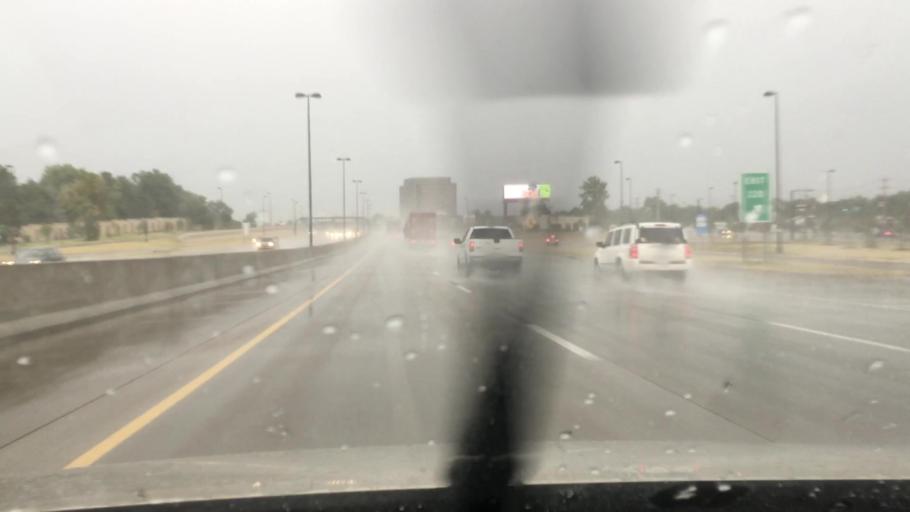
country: US
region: Oklahoma
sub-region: Tulsa County
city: Jenks
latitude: 36.0906
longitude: -95.9379
